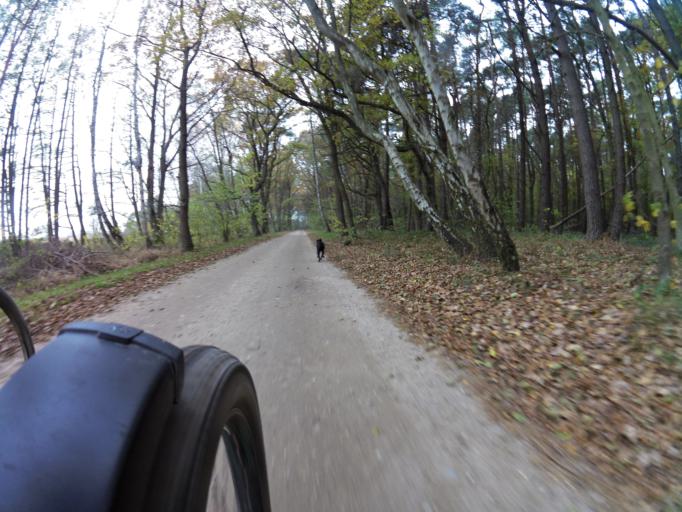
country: PL
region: Pomeranian Voivodeship
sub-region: Powiat pucki
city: Krokowa
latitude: 54.8286
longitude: 18.1209
